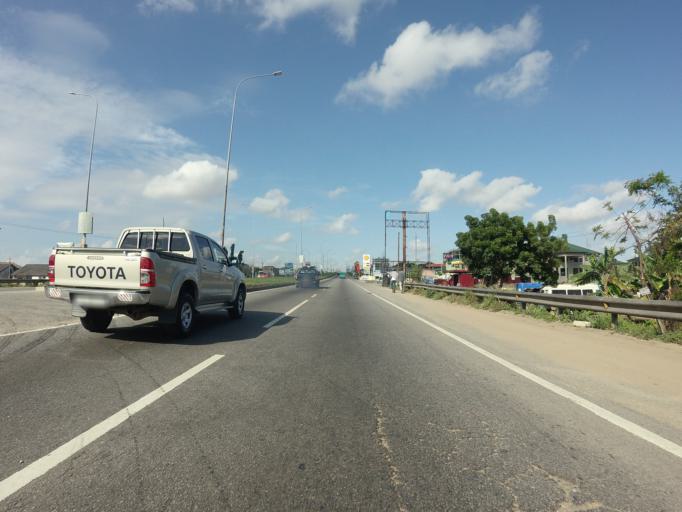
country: GH
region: Central
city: Kasoa
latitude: 5.5457
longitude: -0.3849
